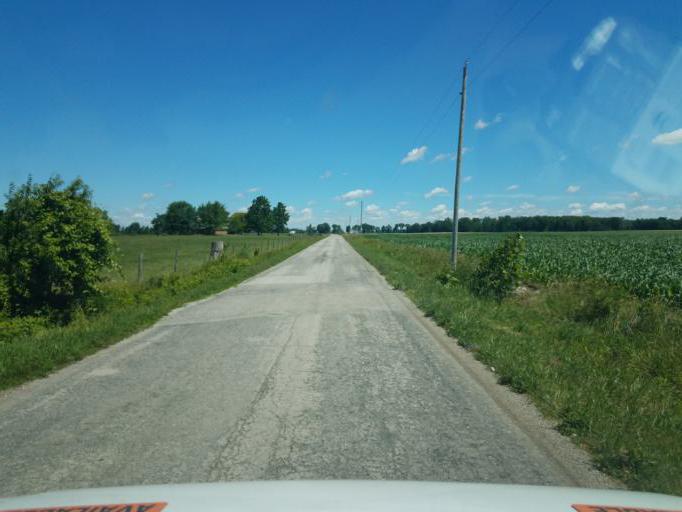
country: US
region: Ohio
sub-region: Morrow County
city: Cardington
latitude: 40.5696
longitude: -82.9382
